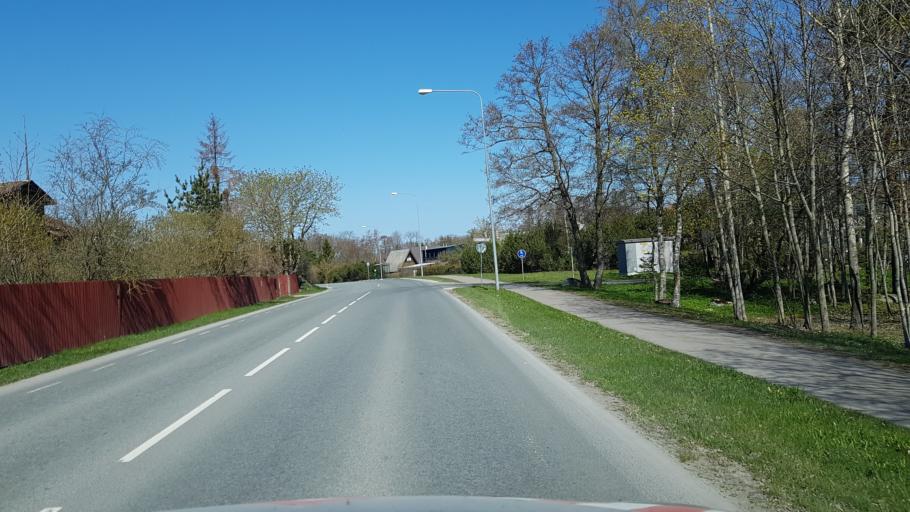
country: EE
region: Harju
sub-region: Viimsi vald
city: Rummu
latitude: 59.5305
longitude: 24.7964
